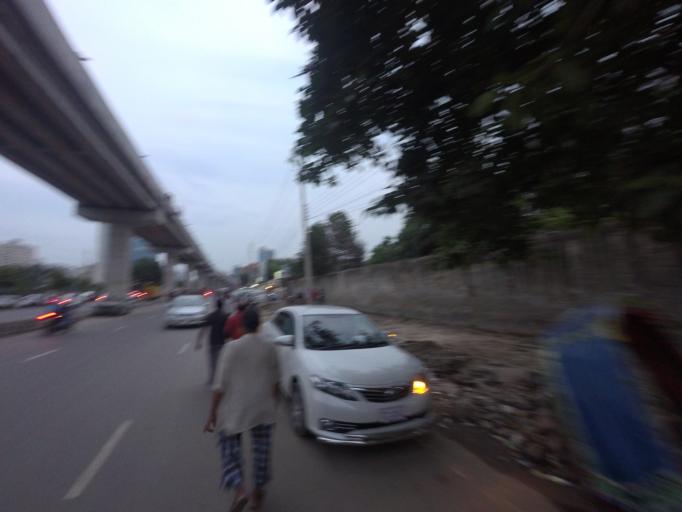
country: BD
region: Dhaka
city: Paltan
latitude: 23.7525
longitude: 90.3990
